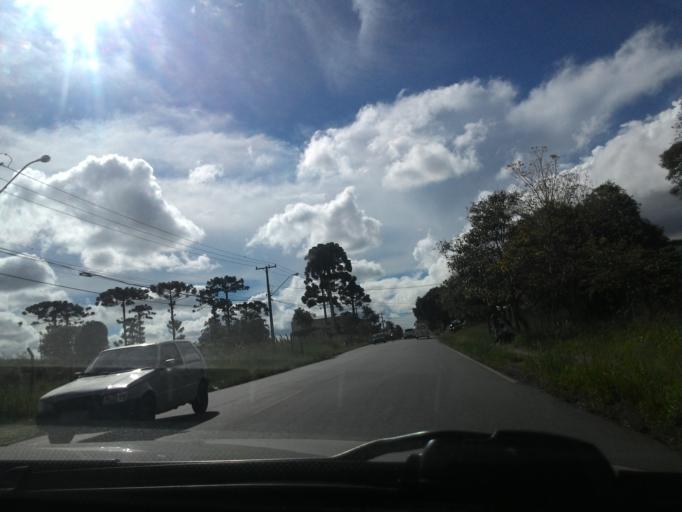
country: BR
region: Parana
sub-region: Sao Jose Dos Pinhais
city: Sao Jose dos Pinhais
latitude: -25.5166
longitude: -49.1926
